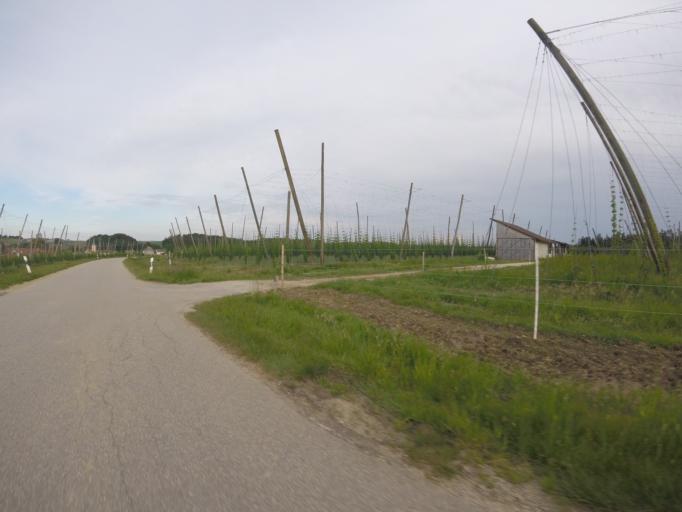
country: DE
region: Bavaria
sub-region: Upper Bavaria
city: Paunzhausen
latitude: 48.4955
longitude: 11.5753
